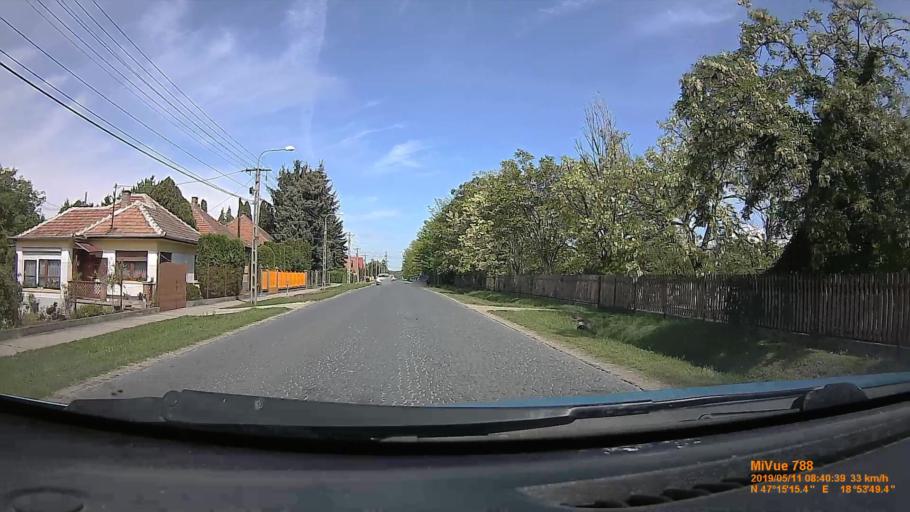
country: HU
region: Fejer
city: Ercsi
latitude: 47.2542
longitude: 18.8971
